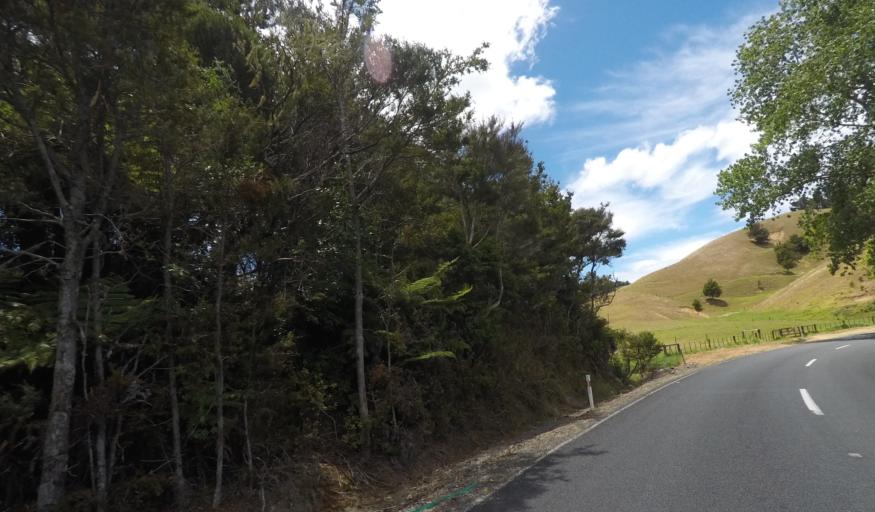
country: NZ
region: Northland
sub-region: Whangarei
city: Ngunguru
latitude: -35.5062
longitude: 174.4398
